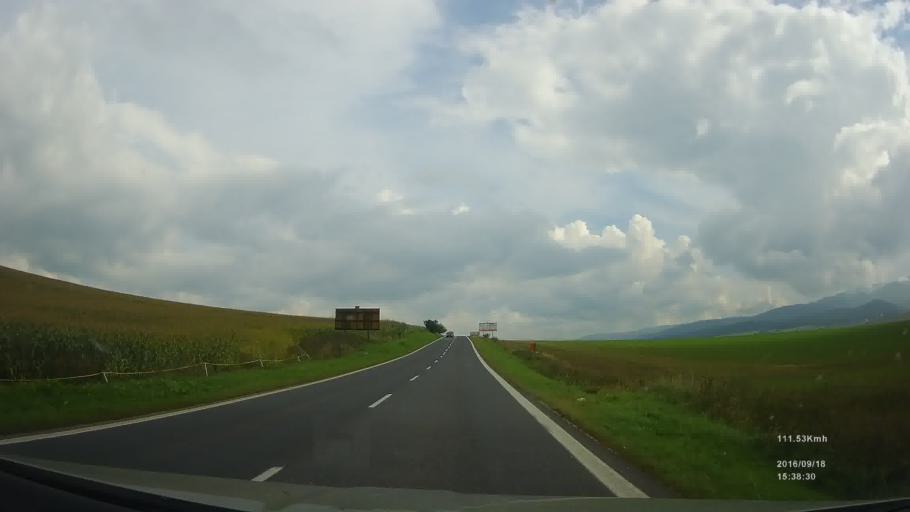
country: SK
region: Kosicky
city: Spisska Nova Ves
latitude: 48.9717
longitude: 20.4938
